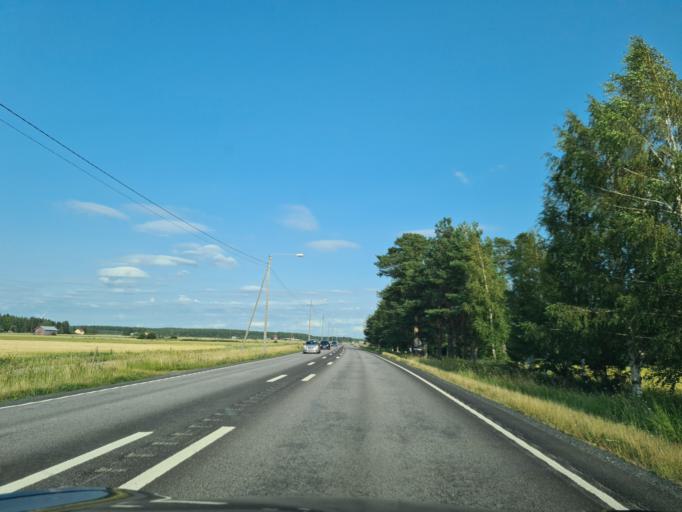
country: FI
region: Ostrobothnia
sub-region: Kyroenmaa
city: Laihia
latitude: 62.9963
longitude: 21.9253
